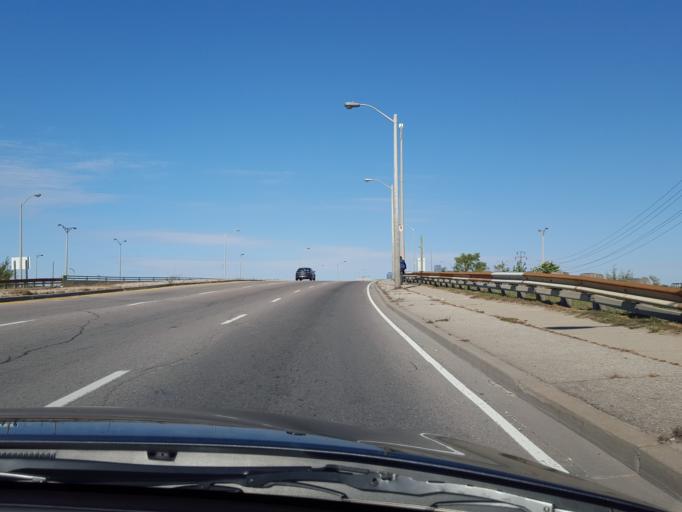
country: CA
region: Ontario
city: Etobicoke
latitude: 43.6168
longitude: -79.5251
